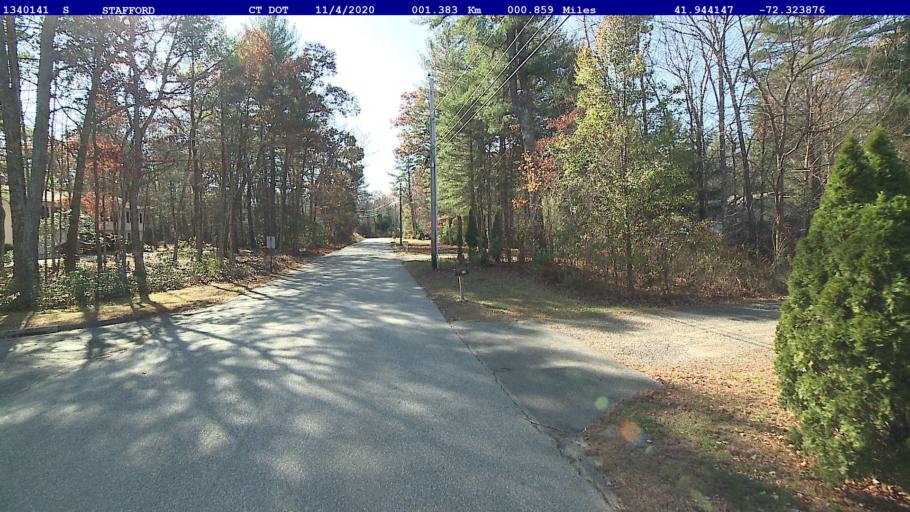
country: US
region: Connecticut
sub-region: Tolland County
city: Stafford Springs
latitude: 41.9441
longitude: -72.3239
